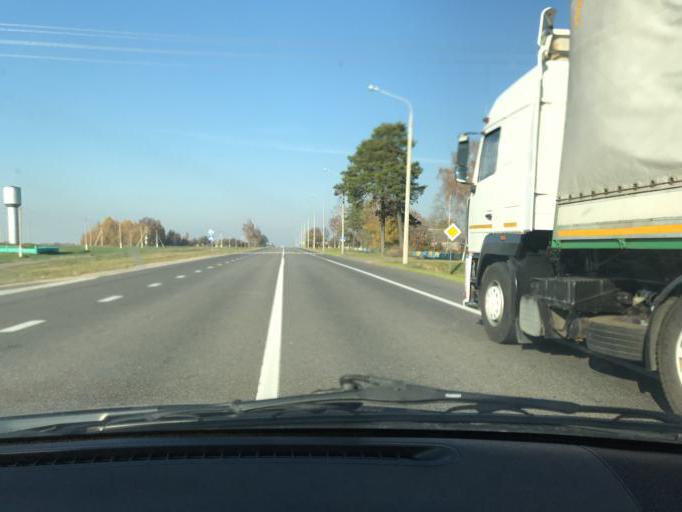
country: BY
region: Vitebsk
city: Orsha
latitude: 54.3334
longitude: 30.4464
